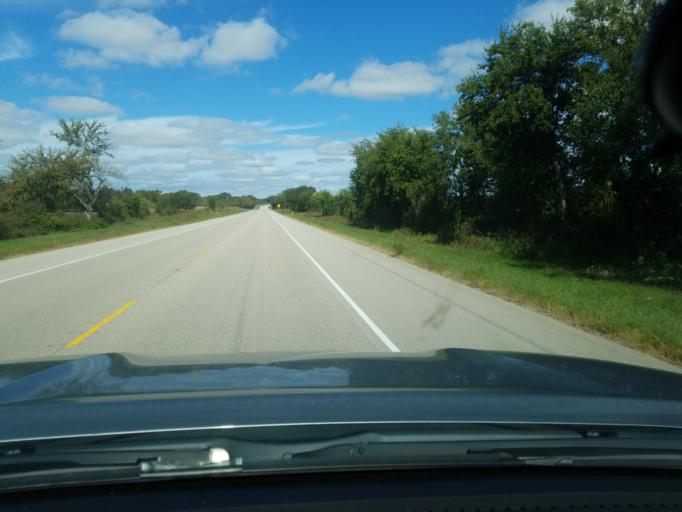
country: US
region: Texas
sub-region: Hamilton County
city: Hamilton
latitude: 31.6038
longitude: -98.1580
